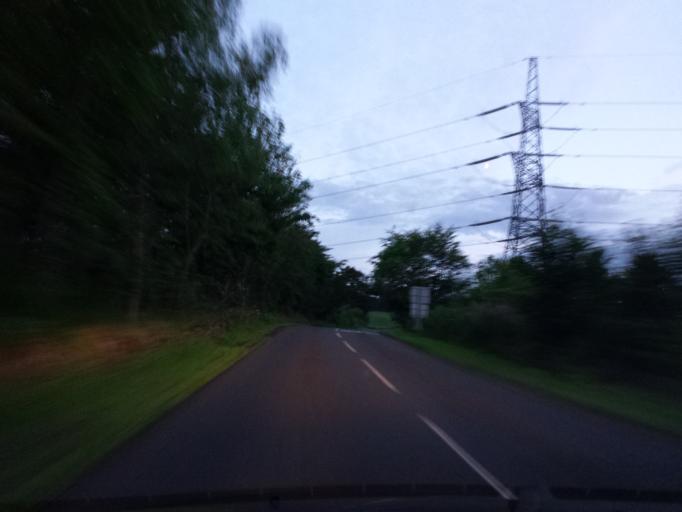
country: GB
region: Scotland
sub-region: The Scottish Borders
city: Duns
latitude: 55.7974
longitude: -2.3369
